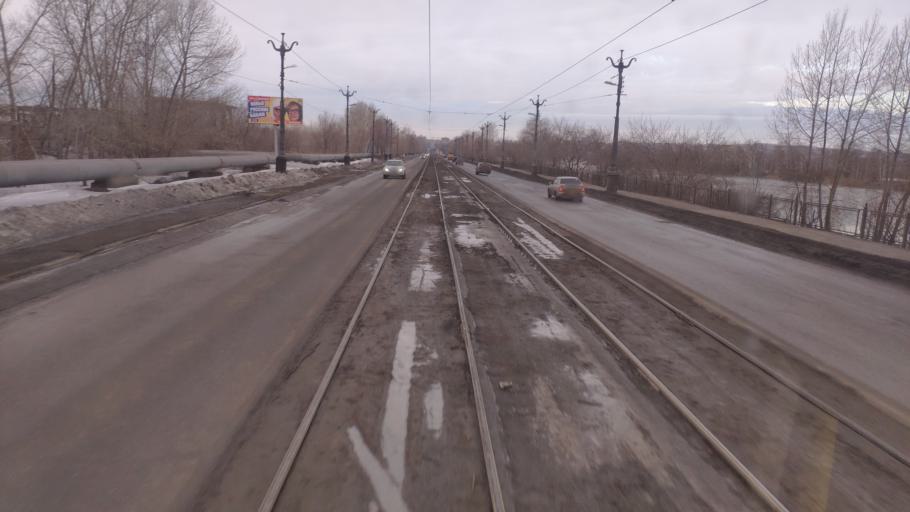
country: RU
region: Chelyabinsk
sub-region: Gorod Magnitogorsk
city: Magnitogorsk
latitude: 53.4222
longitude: 59.0245
